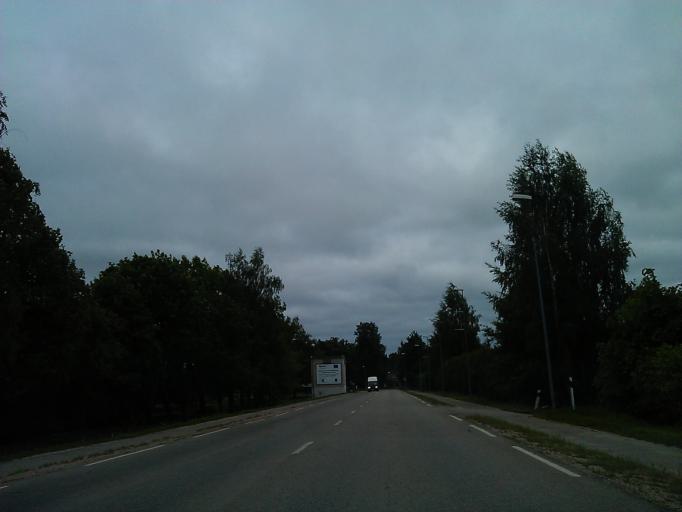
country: LV
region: Carnikava
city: Carnikava
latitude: 57.1283
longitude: 24.2841
